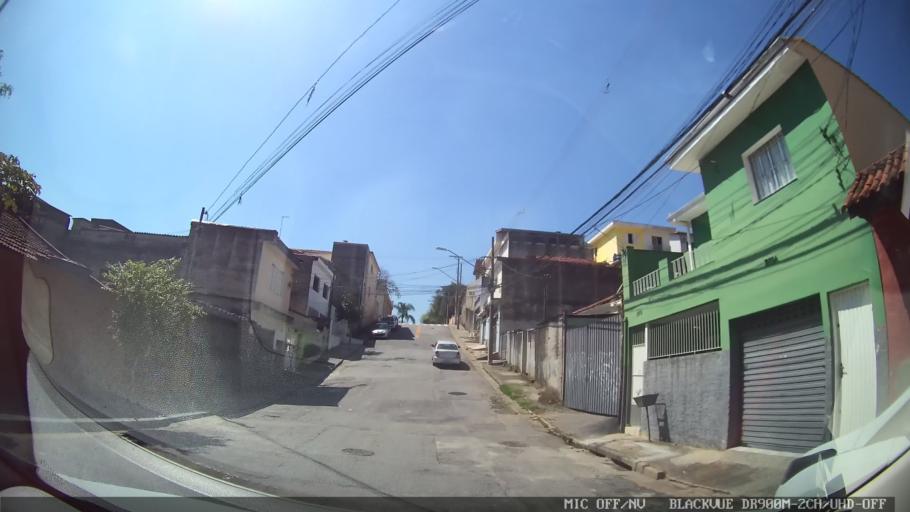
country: BR
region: Sao Paulo
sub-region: Sao Paulo
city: Sao Paulo
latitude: -23.4973
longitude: -46.6570
